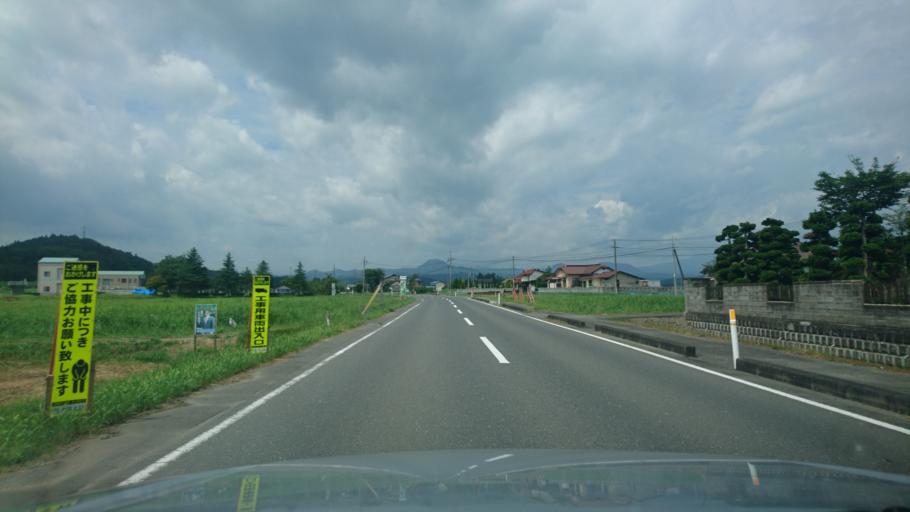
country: JP
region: Iwate
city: Ichinoseki
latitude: 38.8005
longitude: 140.9759
